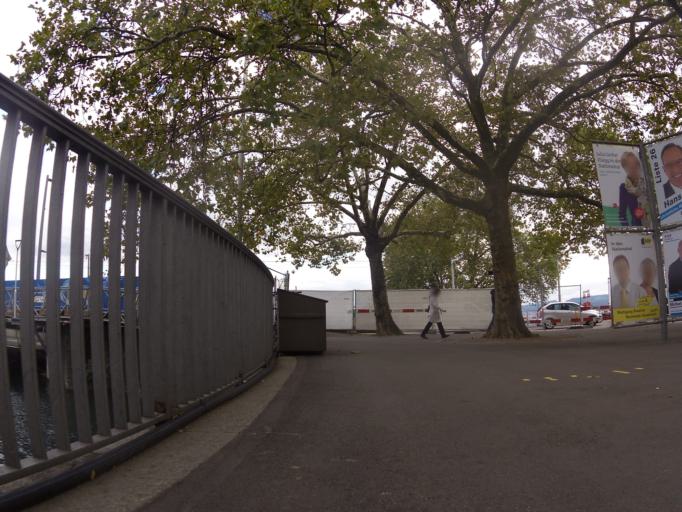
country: CH
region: Zurich
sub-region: Bezirk Zuerich
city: Zuerich (Kreis 1)
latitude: 47.3670
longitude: 8.5419
